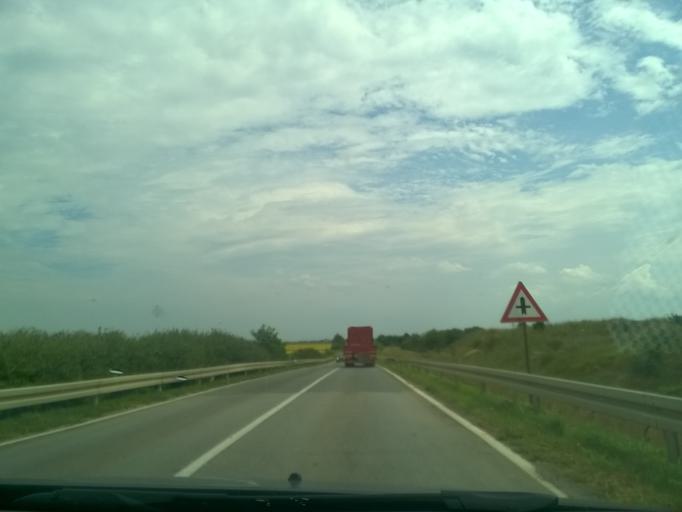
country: RS
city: Klek
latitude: 45.3874
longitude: 20.4961
